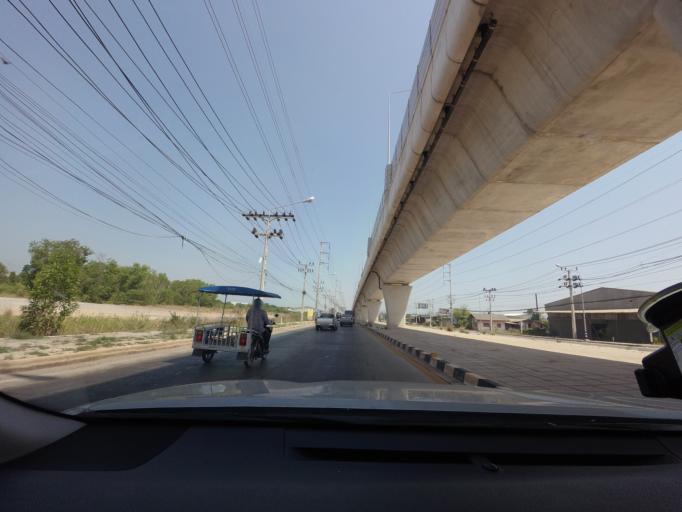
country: TH
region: Surat Thani
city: Surat Thani
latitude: 9.1531
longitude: 99.3692
